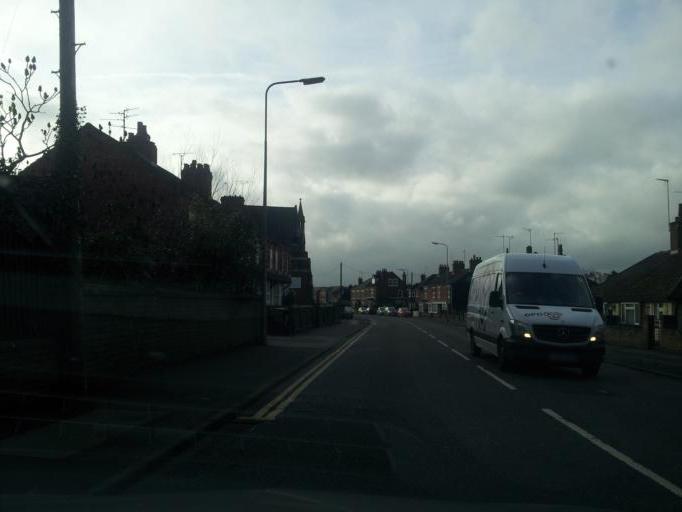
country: GB
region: England
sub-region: Northamptonshire
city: Finedon
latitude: 52.3380
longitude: -0.6524
